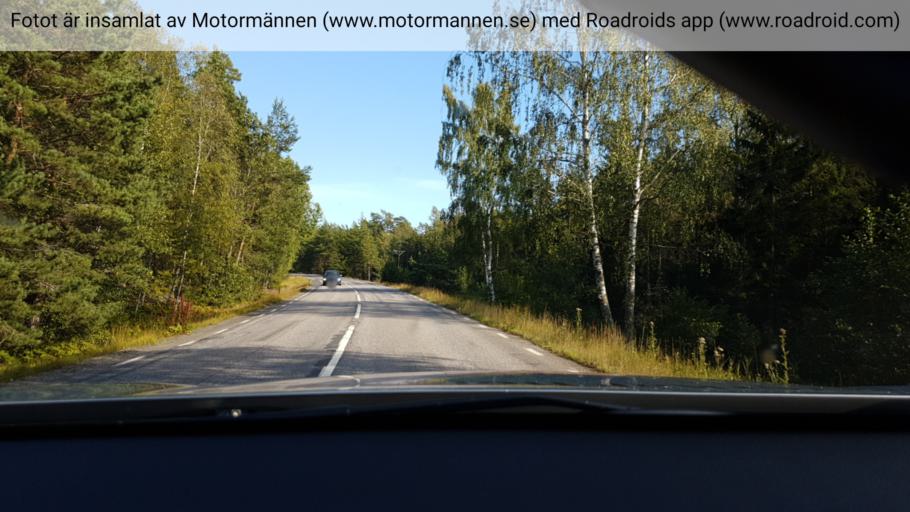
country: SE
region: Stockholm
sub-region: Nynashamns Kommun
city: Nynashamn
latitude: 58.9136
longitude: 17.8893
